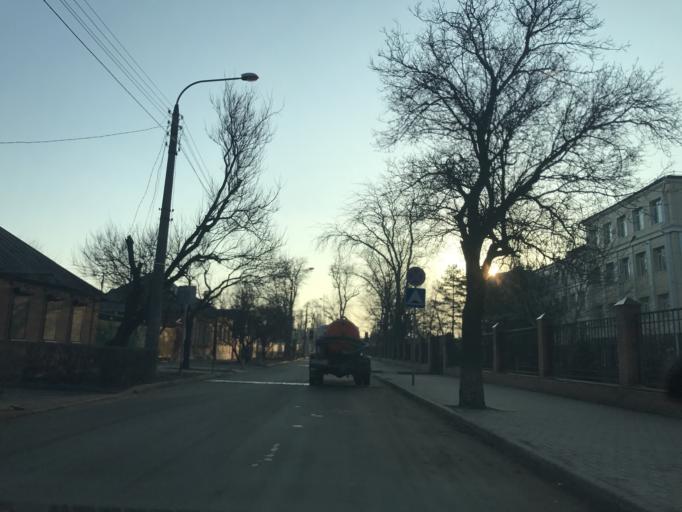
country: RU
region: Rostov
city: Rostov-na-Donu
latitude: 47.2141
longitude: 39.6555
